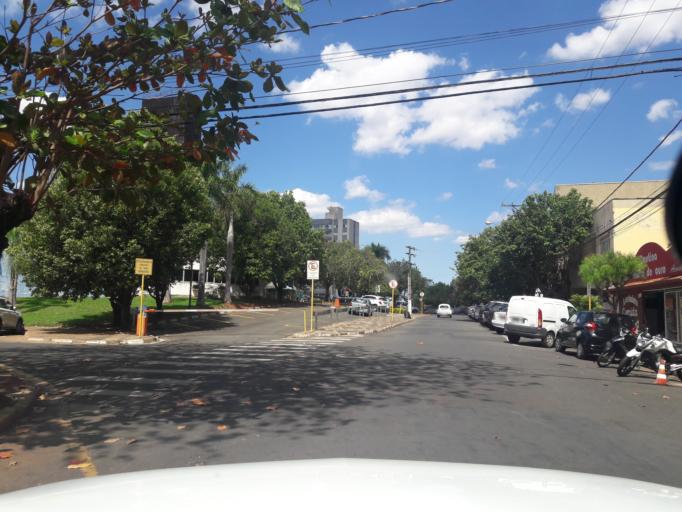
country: BR
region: Sao Paulo
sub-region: Moji-Guacu
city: Mogi-Gaucu
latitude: -22.3682
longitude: -46.9451
